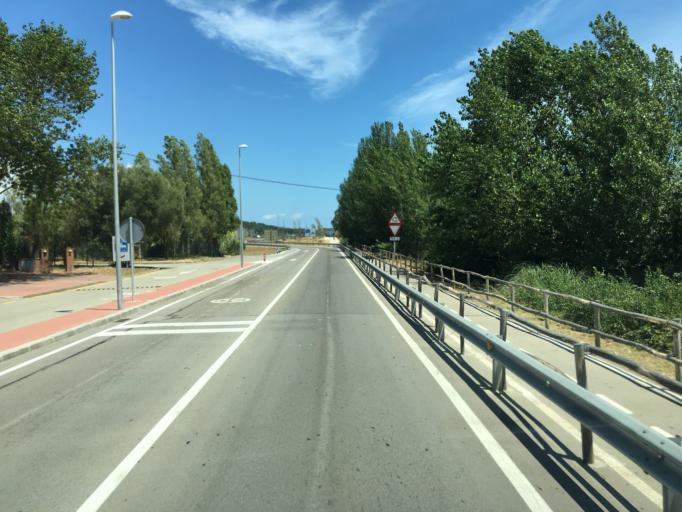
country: ES
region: Catalonia
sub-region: Provincia de Girona
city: Palamos
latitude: 41.8549
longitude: 3.1191
